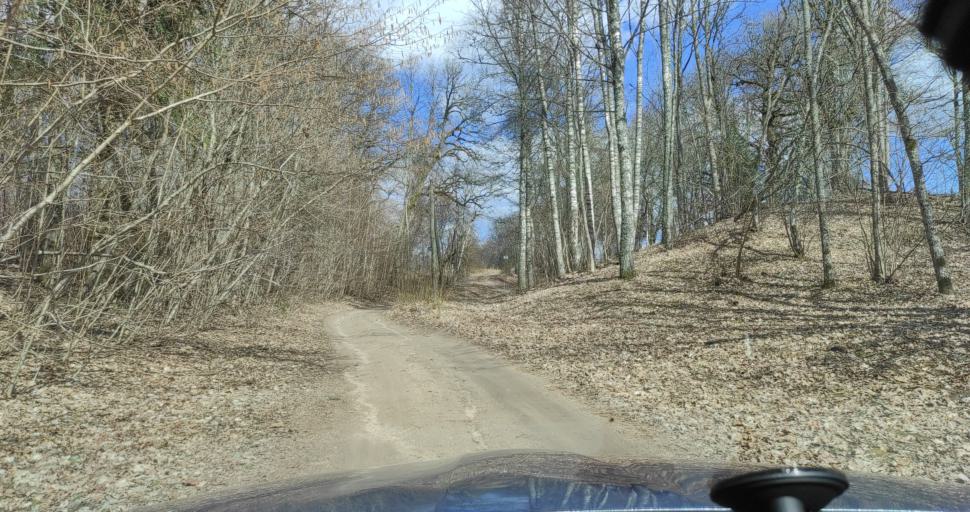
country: LV
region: Kuldigas Rajons
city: Kuldiga
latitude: 56.9598
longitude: 21.9194
